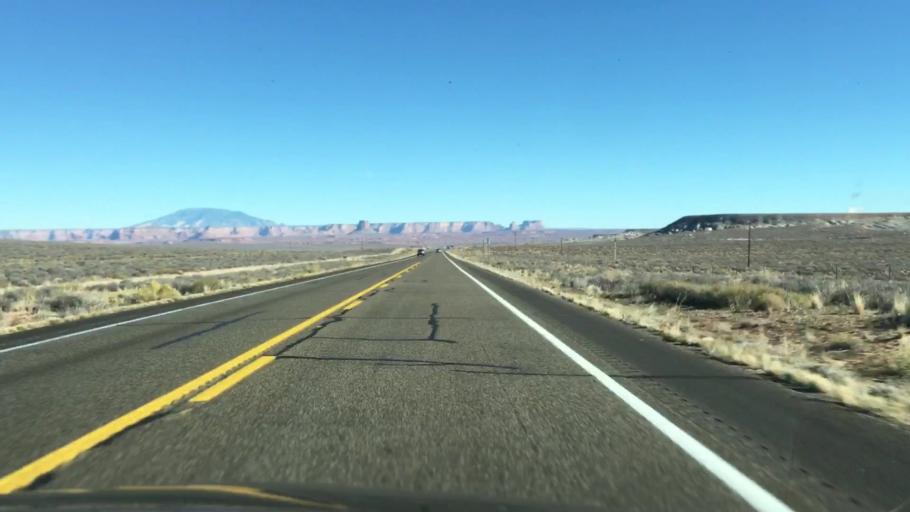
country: US
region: Arizona
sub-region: Coconino County
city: Page
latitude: 36.9819
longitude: -111.5426
